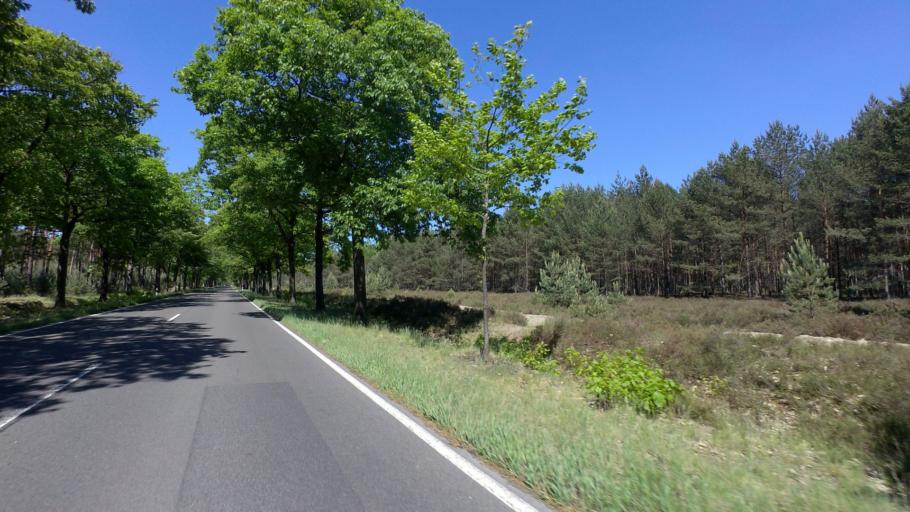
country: DE
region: Brandenburg
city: Drachhausen
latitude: 51.9041
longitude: 14.3551
